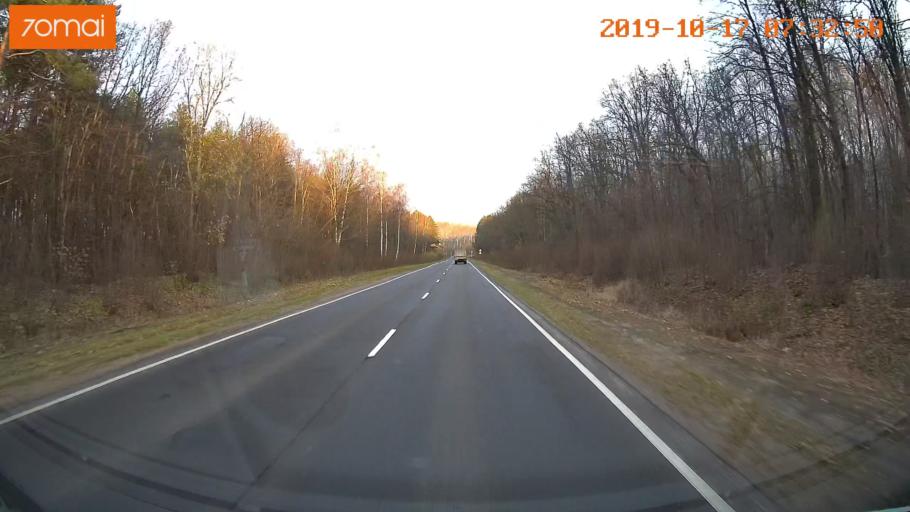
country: RU
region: Ivanovo
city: Gavrilov Posad
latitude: 56.3997
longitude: 39.9667
